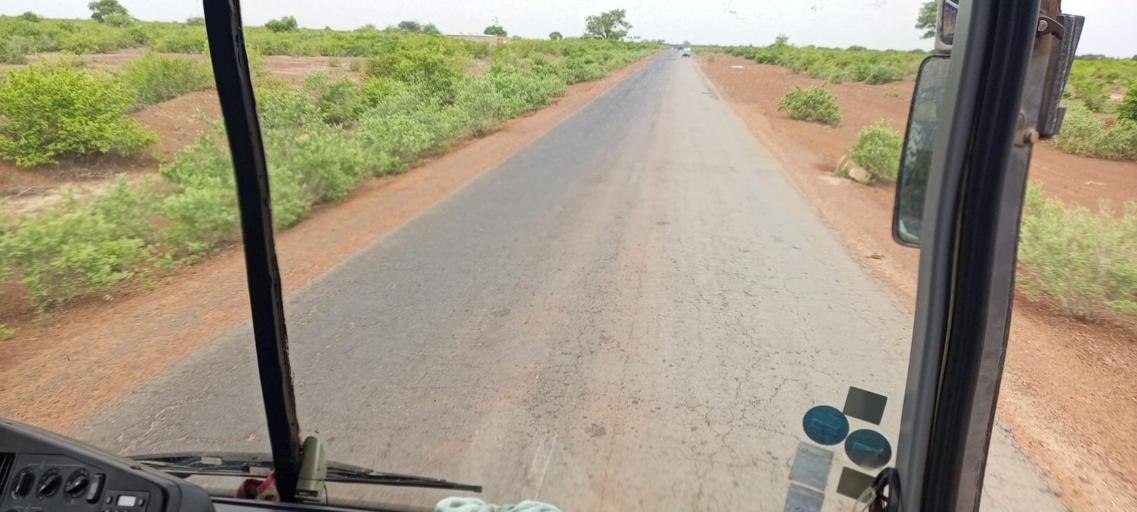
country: ML
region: Segou
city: Bla
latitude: 12.7579
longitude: -5.7368
